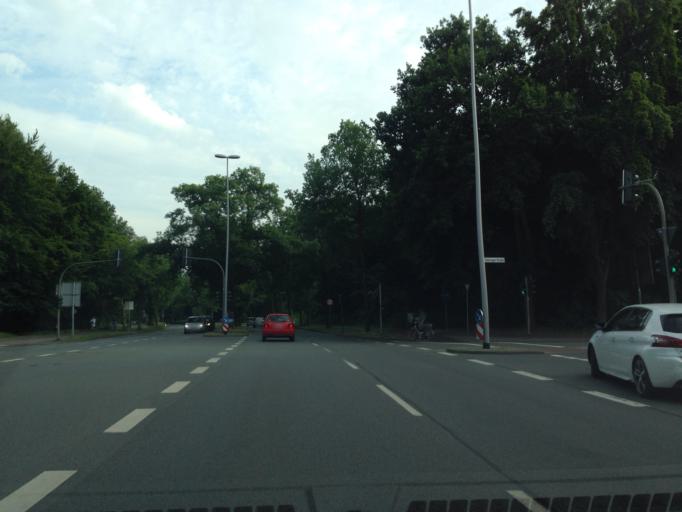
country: DE
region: North Rhine-Westphalia
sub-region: Regierungsbezirk Munster
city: Muenster
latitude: 51.9556
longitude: 7.6027
